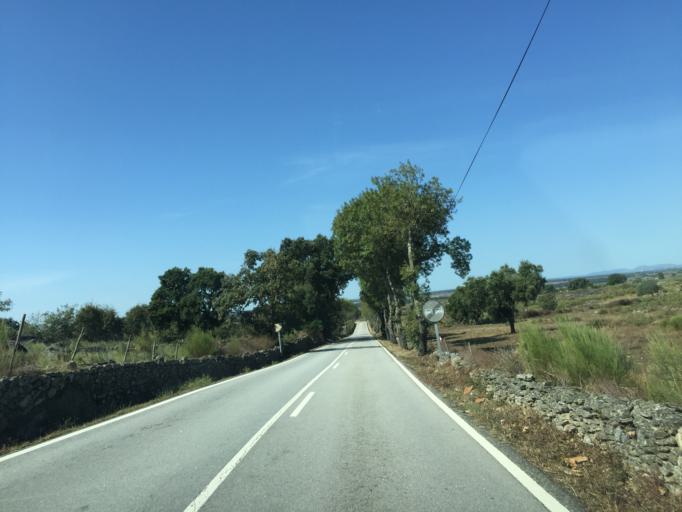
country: PT
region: Portalegre
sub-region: Portalegre
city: Alagoa
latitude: 39.4392
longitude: -7.5558
